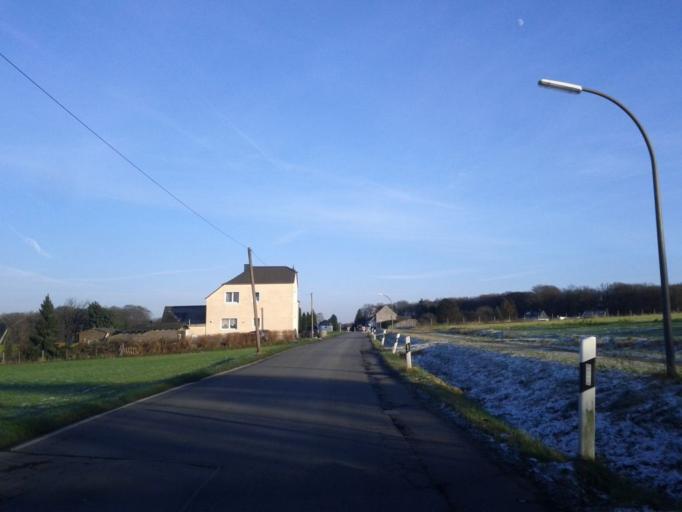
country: DE
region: North Rhine-Westphalia
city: Lanstrop
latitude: 51.5778
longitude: 7.5762
